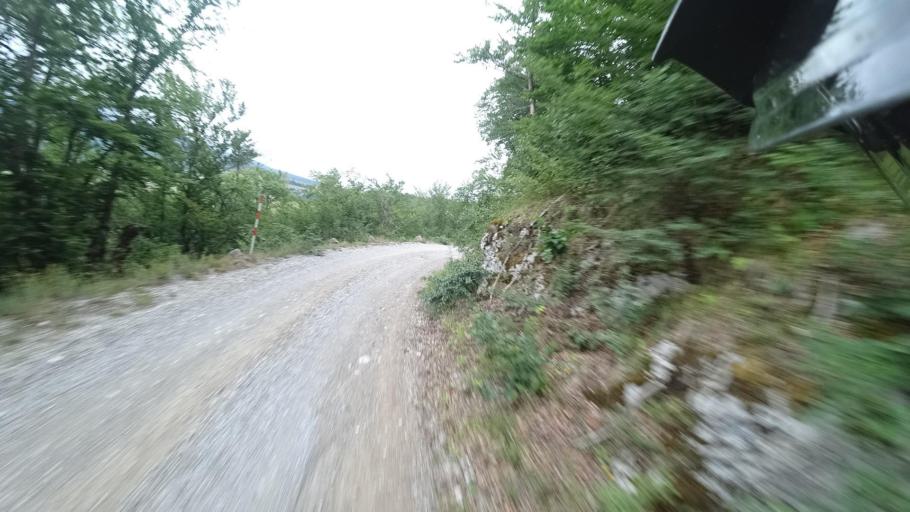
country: HR
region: Zadarska
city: Gracac
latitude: 44.5165
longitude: 15.8641
